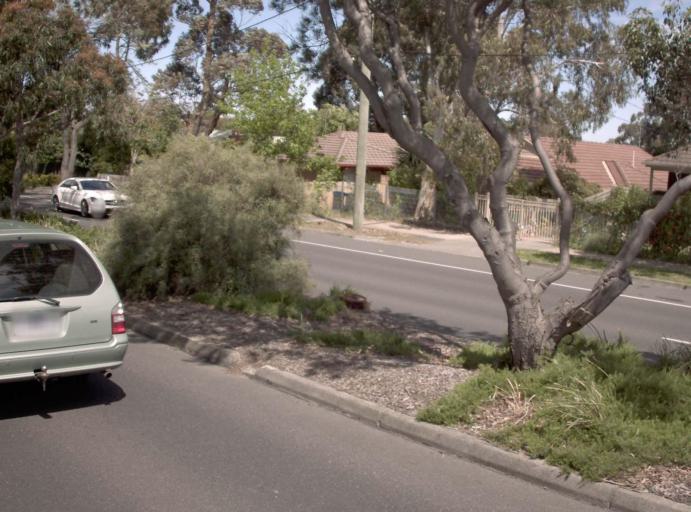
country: AU
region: Victoria
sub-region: Whitehorse
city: Blackburn South
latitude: -37.8441
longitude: 145.1549
